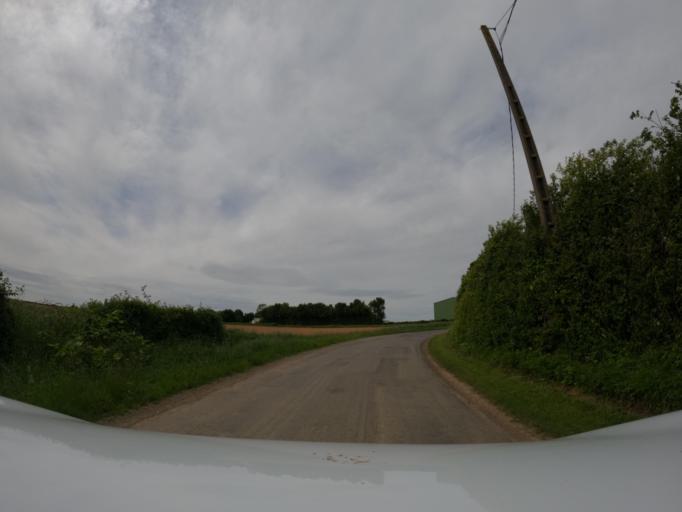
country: FR
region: Pays de la Loire
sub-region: Departement de la Vendee
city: Saint-Hilaire-des-Loges
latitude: 46.4921
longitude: -0.6336
